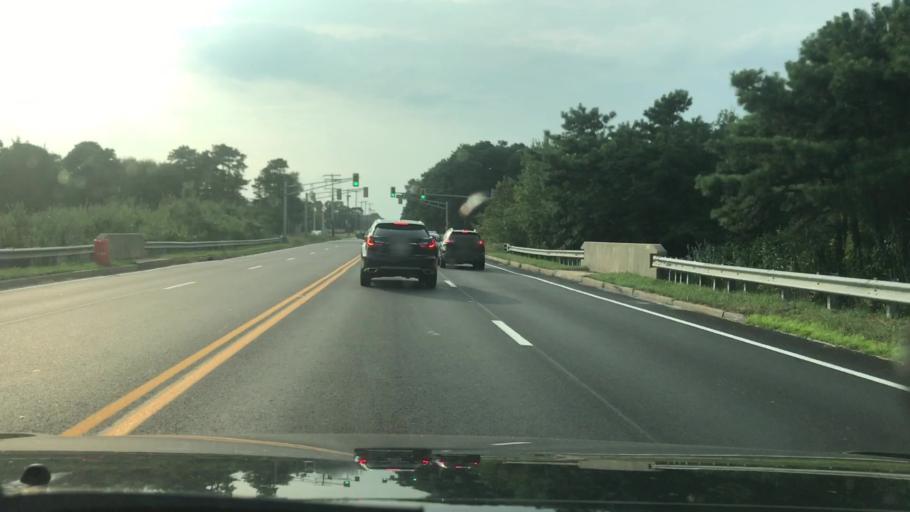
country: US
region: New Jersey
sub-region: Ocean County
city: Leisure Village
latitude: 40.0707
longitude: -74.1718
